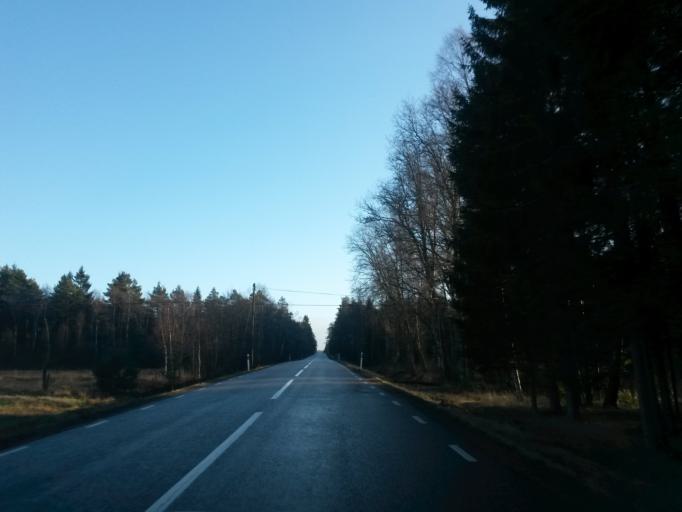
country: SE
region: Vaestra Goetaland
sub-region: Vargarda Kommun
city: Vargarda
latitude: 57.9187
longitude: 12.8760
